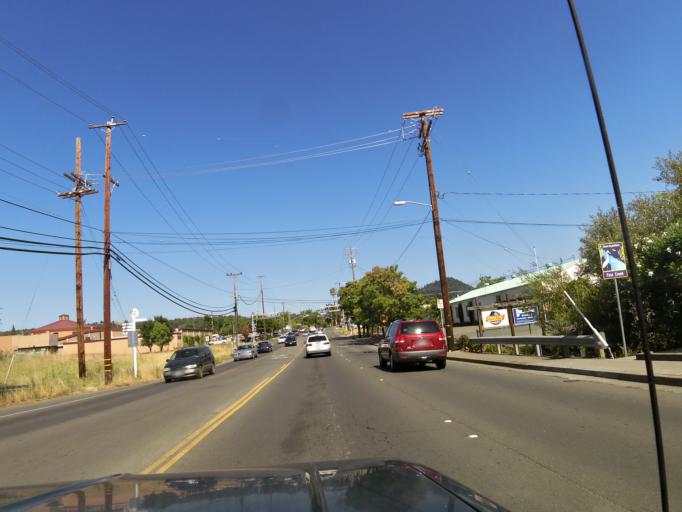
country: US
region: California
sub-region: Sonoma County
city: Healdsburg
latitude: 38.6262
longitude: -122.8755
